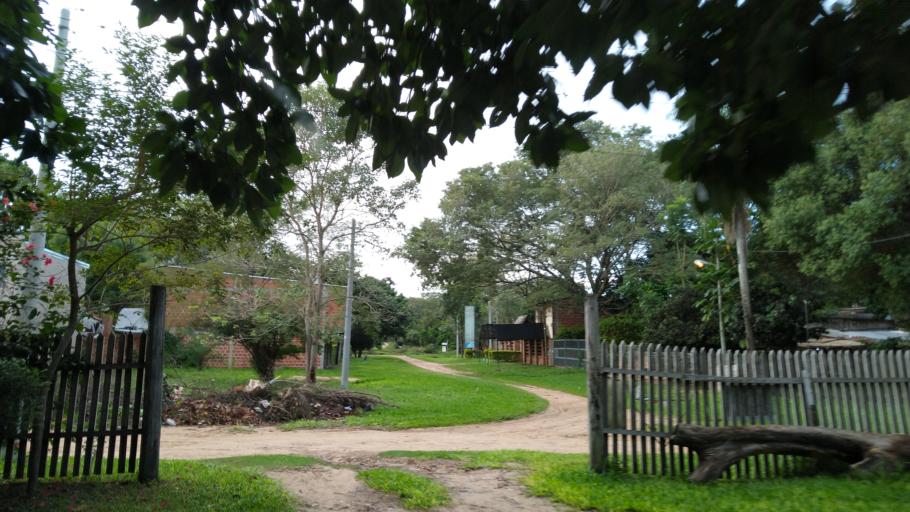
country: AR
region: Corrientes
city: Ituzaingo
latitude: -27.5898
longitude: -56.7051
